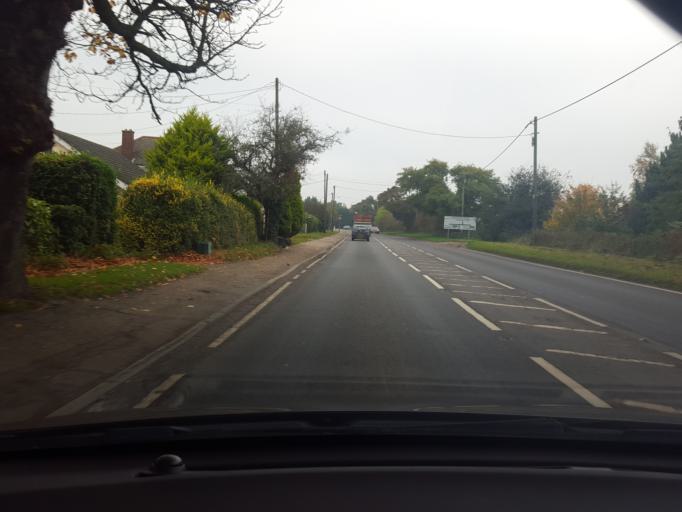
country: GB
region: England
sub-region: Essex
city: Brightlingsea
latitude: 51.8401
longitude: 1.0280
